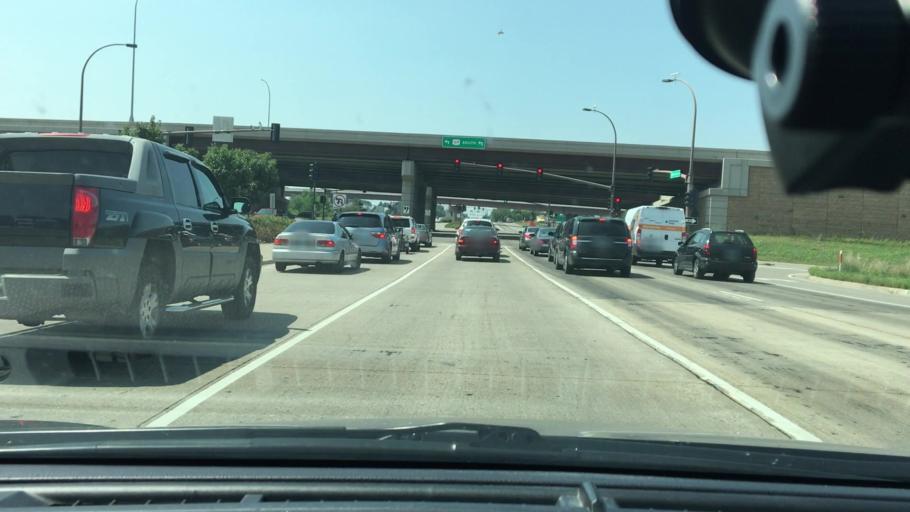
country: US
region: Minnesota
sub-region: Hennepin County
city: Osseo
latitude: 45.1090
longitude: -93.3902
